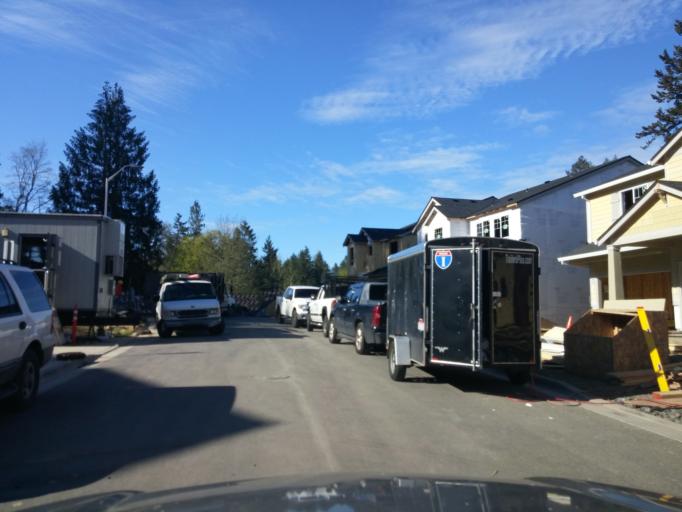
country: US
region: Oregon
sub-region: Washington County
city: Cedar Mill
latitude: 45.5355
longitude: -122.7967
